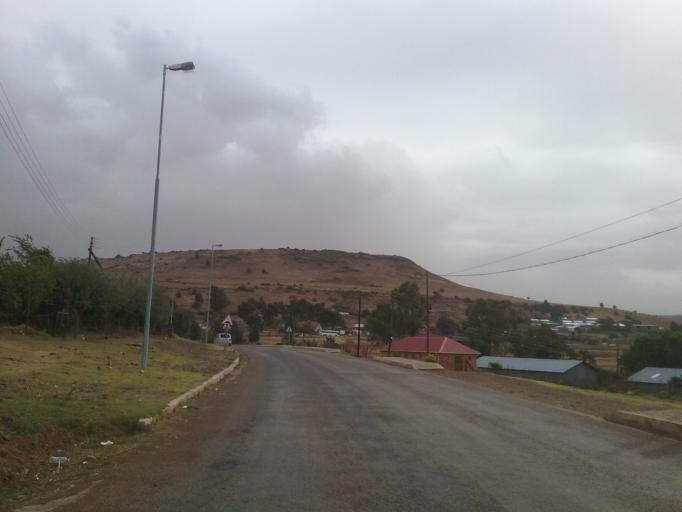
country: LS
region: Quthing
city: Quthing
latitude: -30.4092
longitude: 27.7002
